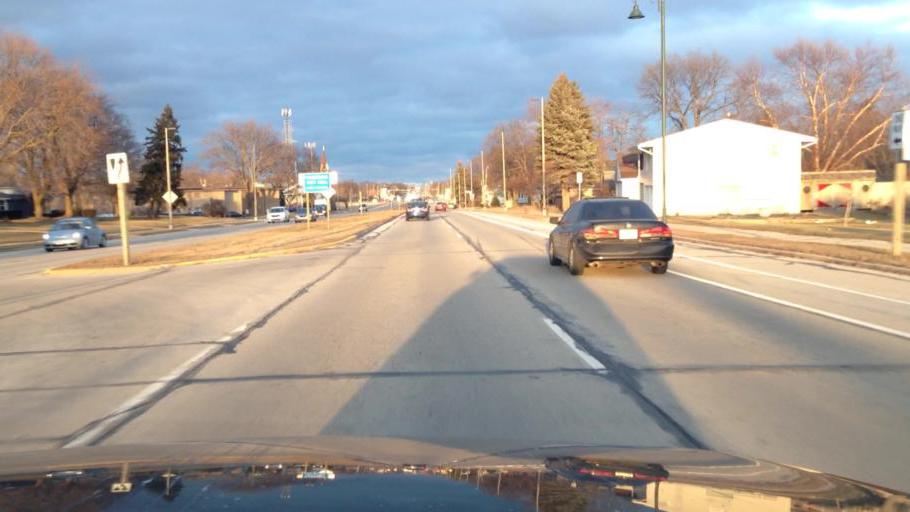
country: US
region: Wisconsin
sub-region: Milwaukee County
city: Greenfield
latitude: 42.9670
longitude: -88.0035
